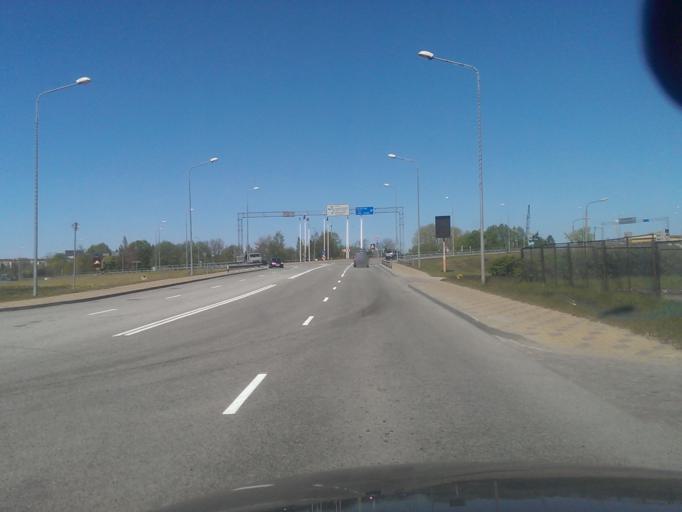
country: LV
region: Ventspils
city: Ventspils
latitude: 57.3858
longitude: 21.5867
